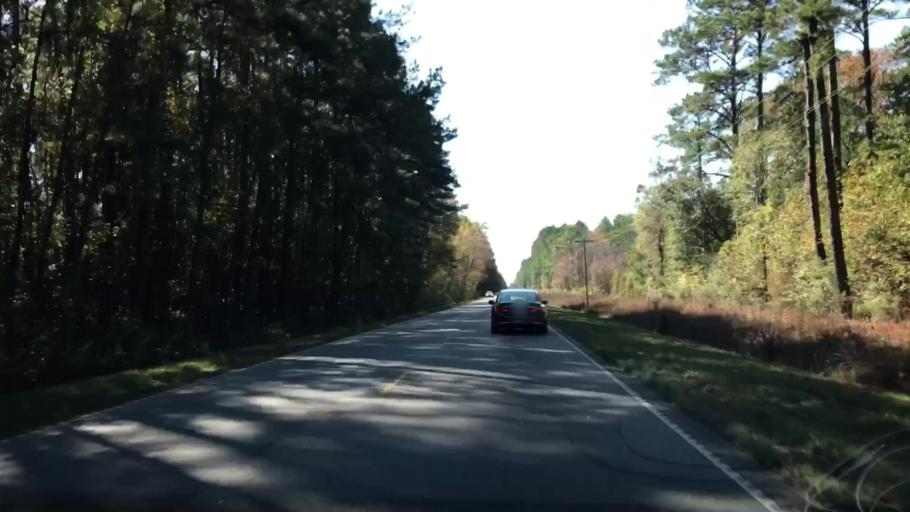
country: US
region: South Carolina
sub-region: Jasper County
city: Ridgeland
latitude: 32.3734
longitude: -80.9141
